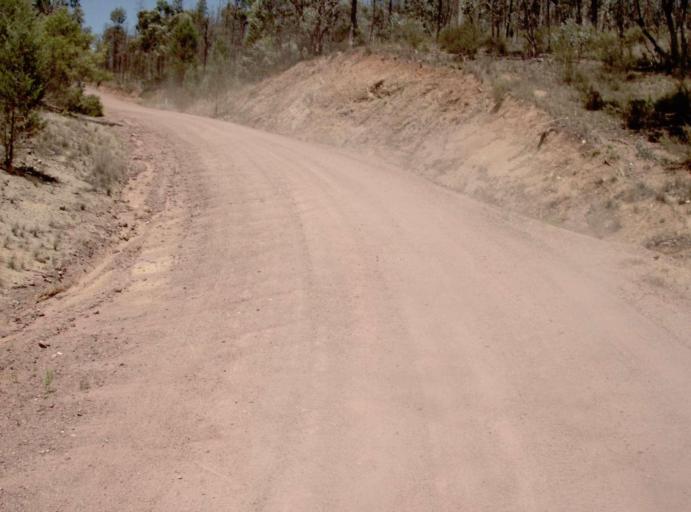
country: AU
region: New South Wales
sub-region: Snowy River
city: Jindabyne
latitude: -36.9186
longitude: 148.3967
